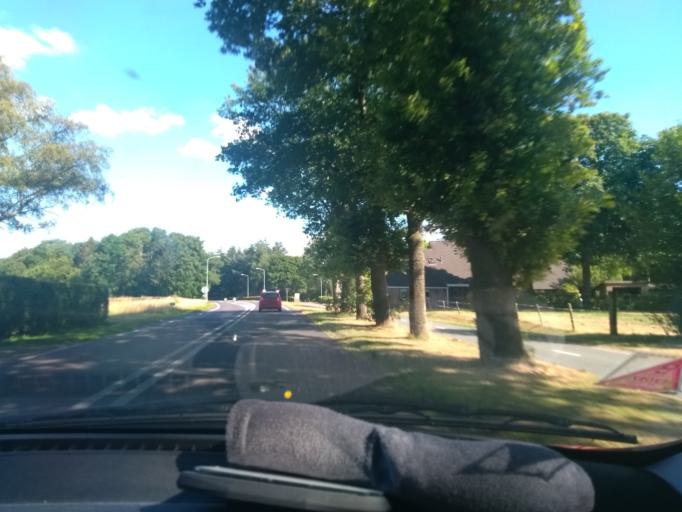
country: NL
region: Drenthe
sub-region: Gemeente Tynaarlo
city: Vries
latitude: 53.0838
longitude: 6.5680
